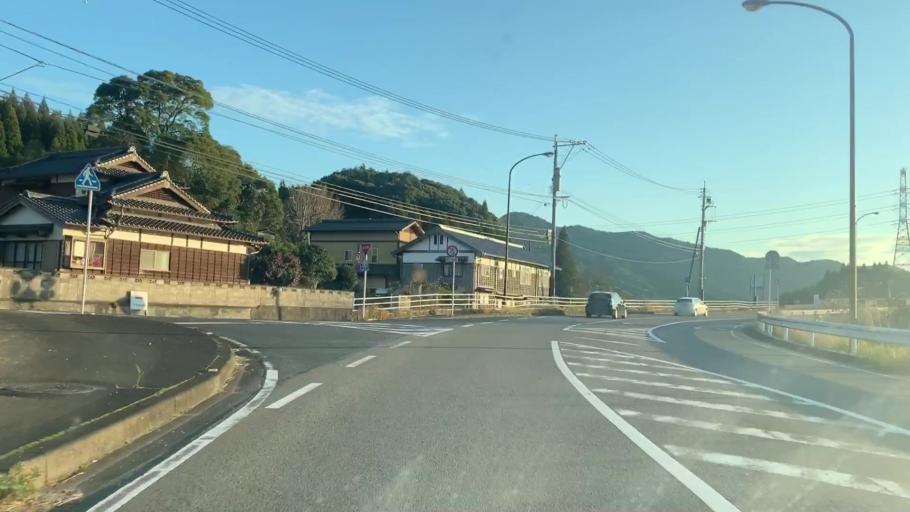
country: JP
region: Saga Prefecture
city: Karatsu
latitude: 33.3493
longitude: 129.9930
